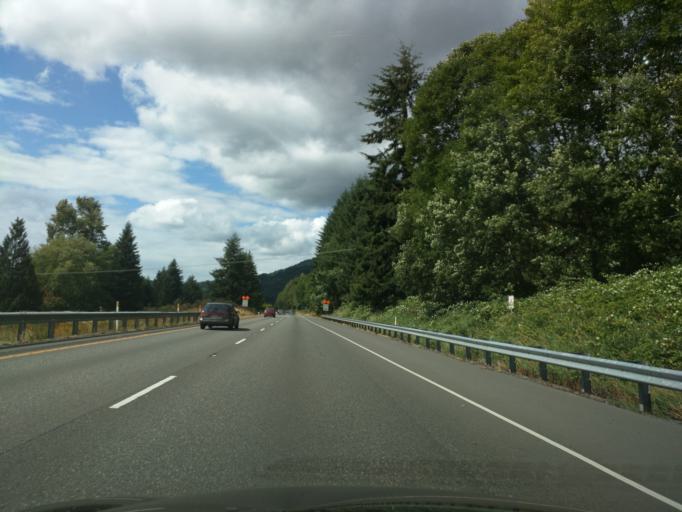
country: US
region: Washington
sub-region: Whatcom County
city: Sudden Valley
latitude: 48.6537
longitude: -122.3677
